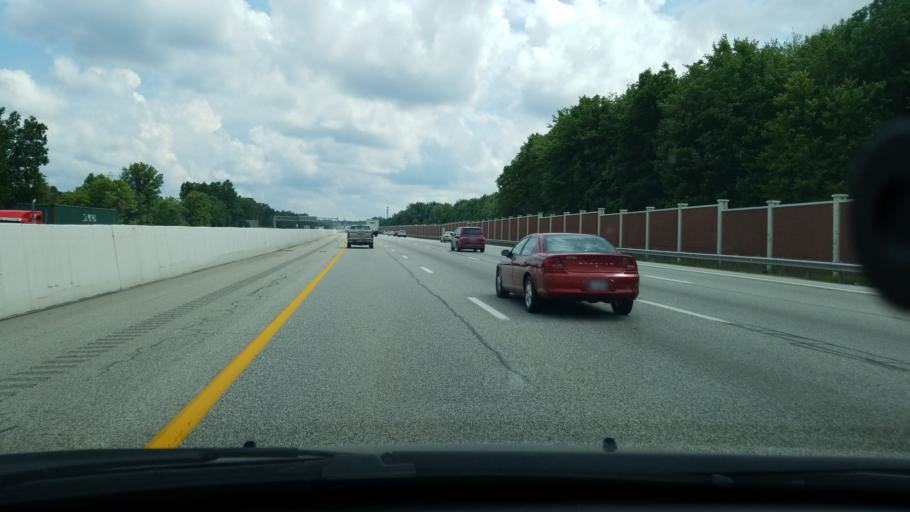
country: US
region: Ohio
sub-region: Cuyahoga County
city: Independence
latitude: 41.3746
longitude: -81.6526
